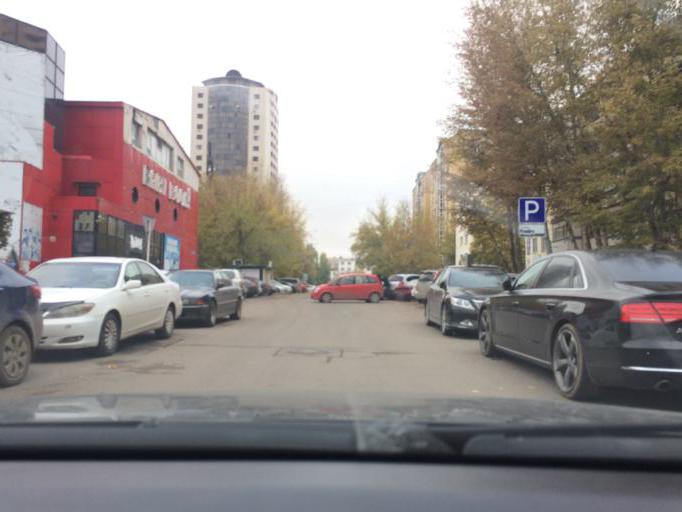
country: KZ
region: Astana Qalasy
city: Astana
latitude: 51.1644
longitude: 71.4381
